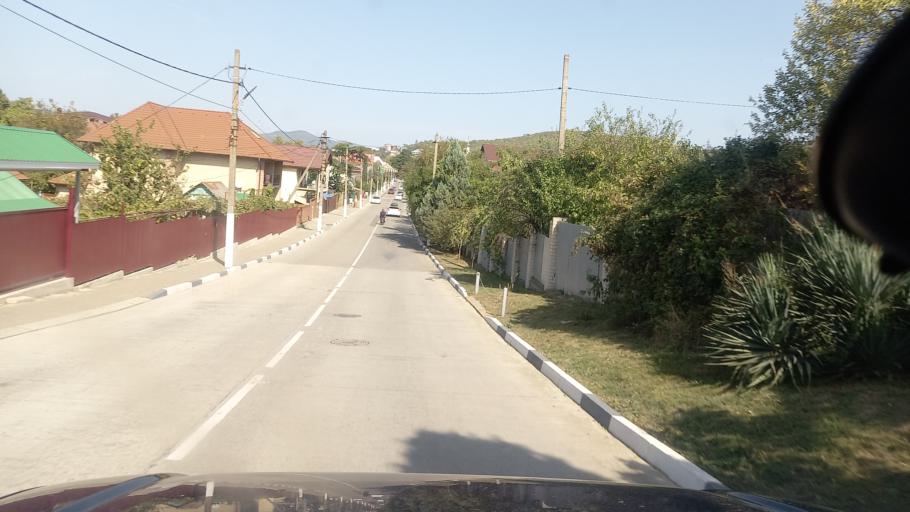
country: RU
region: Krasnodarskiy
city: Arkhipo-Osipovka
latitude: 44.3669
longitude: 38.5316
